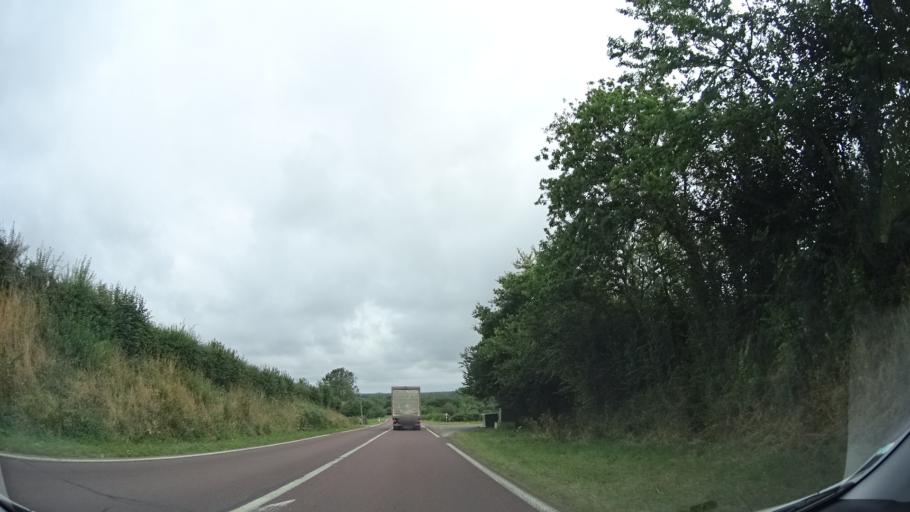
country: FR
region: Lower Normandy
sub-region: Departement de la Manche
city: Gouville-sur-Mer
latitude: 49.1340
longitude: -1.5036
